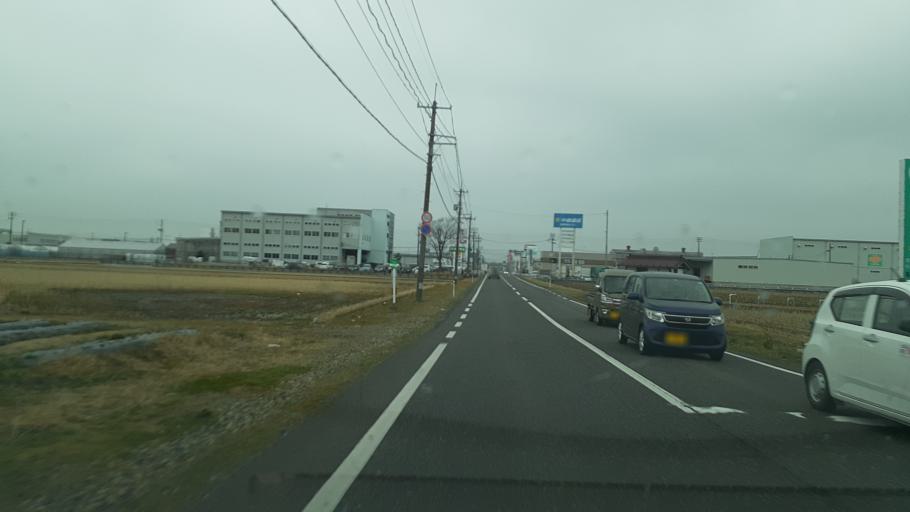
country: JP
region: Niigata
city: Kameda-honcho
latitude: 37.8664
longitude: 139.0792
